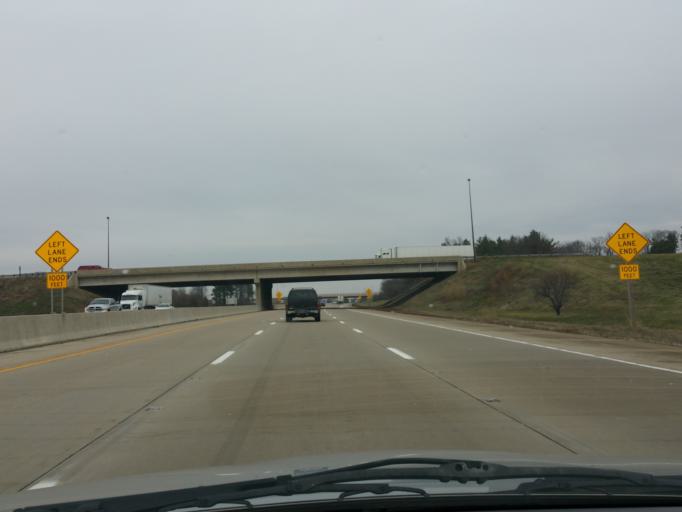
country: US
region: Wisconsin
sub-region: Rock County
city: Beloit
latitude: 42.4903
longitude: -88.9945
